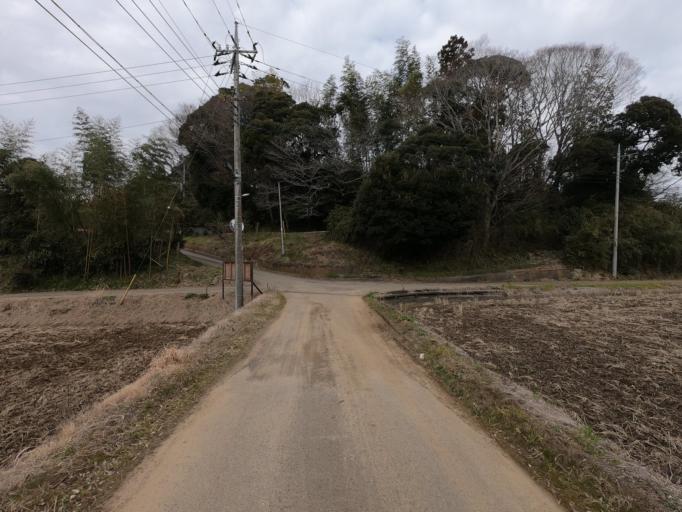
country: JP
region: Ibaraki
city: Itako
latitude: 36.0606
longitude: 140.4493
